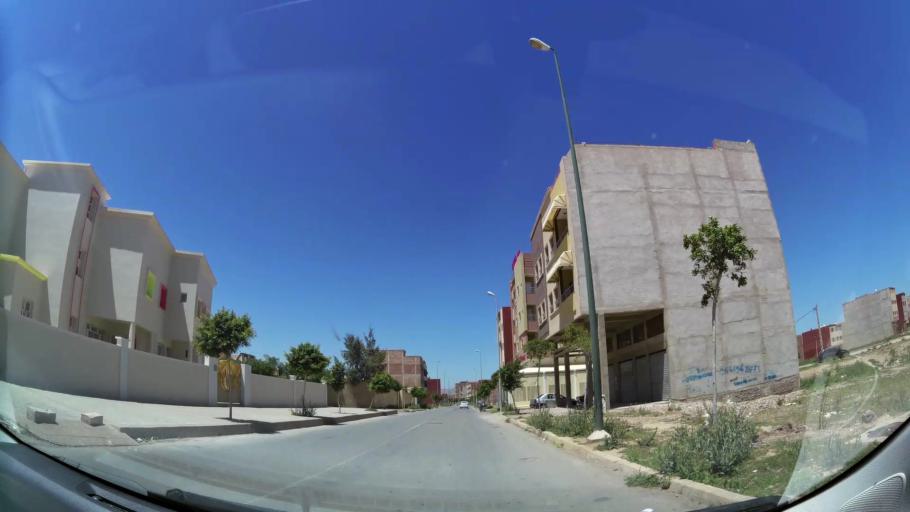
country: MA
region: Oriental
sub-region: Oujda-Angad
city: Oujda
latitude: 34.6690
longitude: -1.8761
